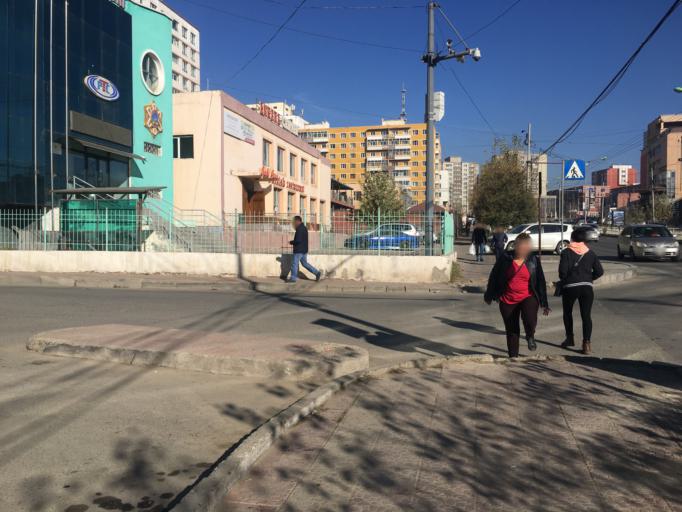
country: MN
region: Ulaanbaatar
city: Ulaanbaatar
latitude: 47.9209
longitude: 106.8904
